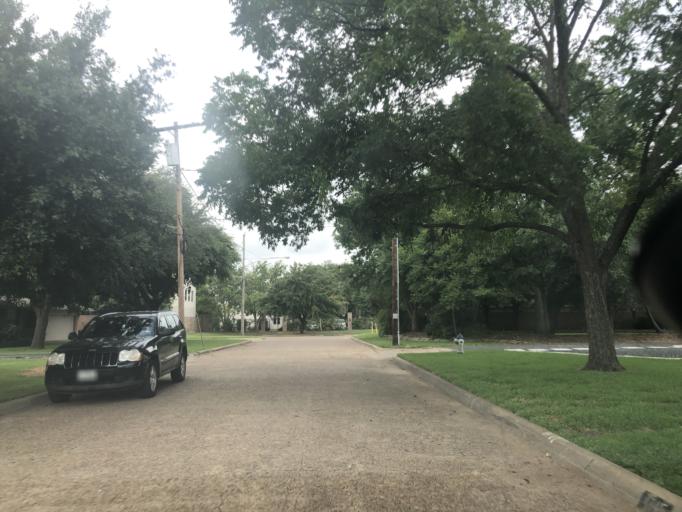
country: US
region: Texas
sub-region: Dallas County
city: University Park
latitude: 32.8655
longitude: -96.8401
